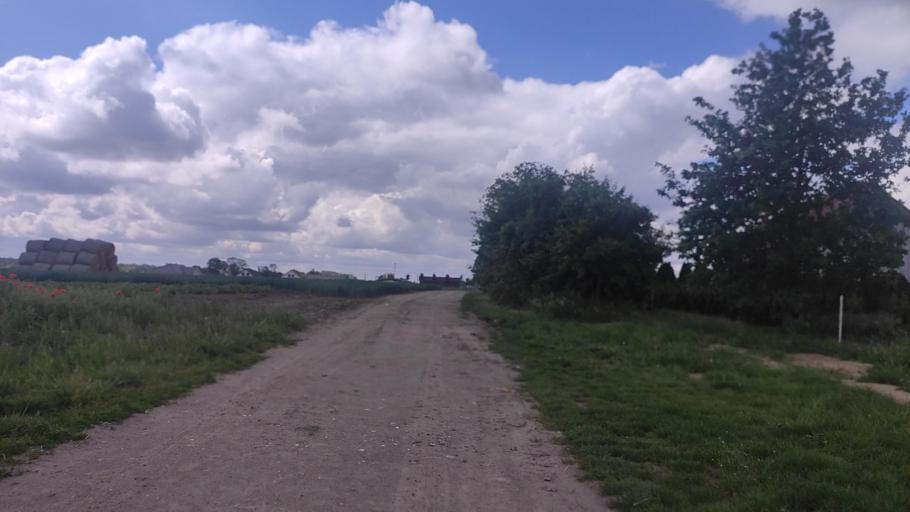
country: PL
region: Greater Poland Voivodeship
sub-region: Powiat poznanski
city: Kostrzyn
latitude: 52.4169
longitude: 17.1739
